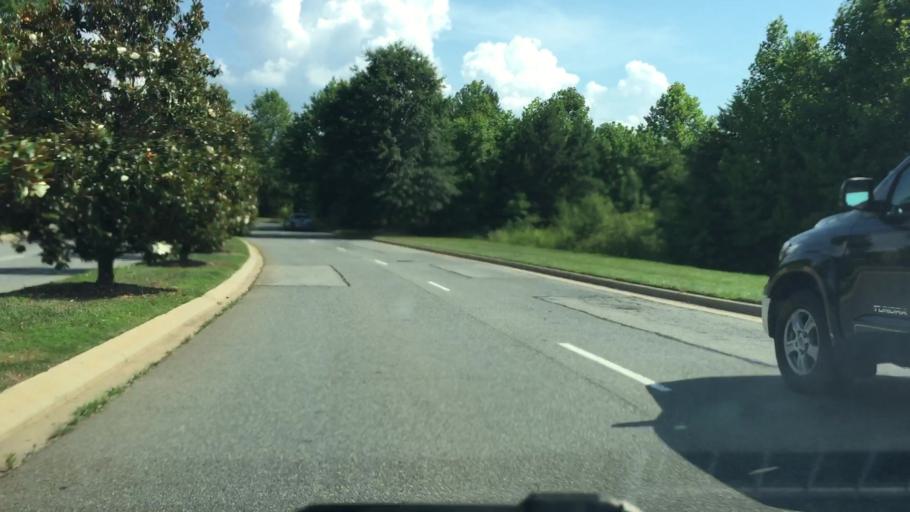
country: US
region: North Carolina
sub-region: Iredell County
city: Mooresville
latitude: 35.5852
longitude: -80.8829
